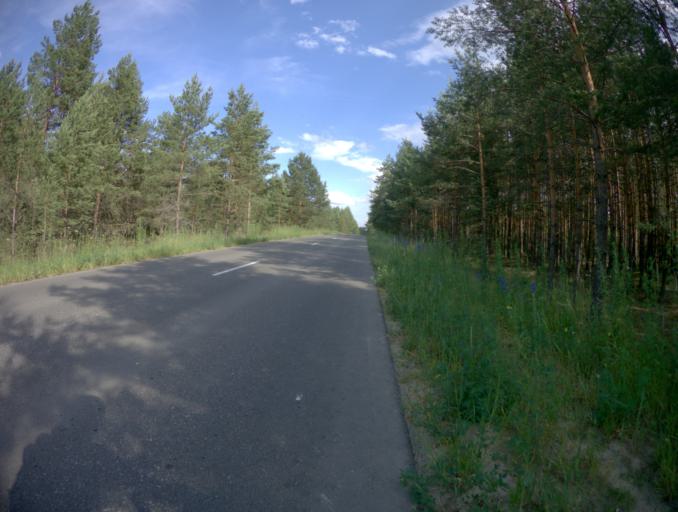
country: RU
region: Nizjnij Novgorod
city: Frolishchi
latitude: 56.3473
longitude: 42.7467
